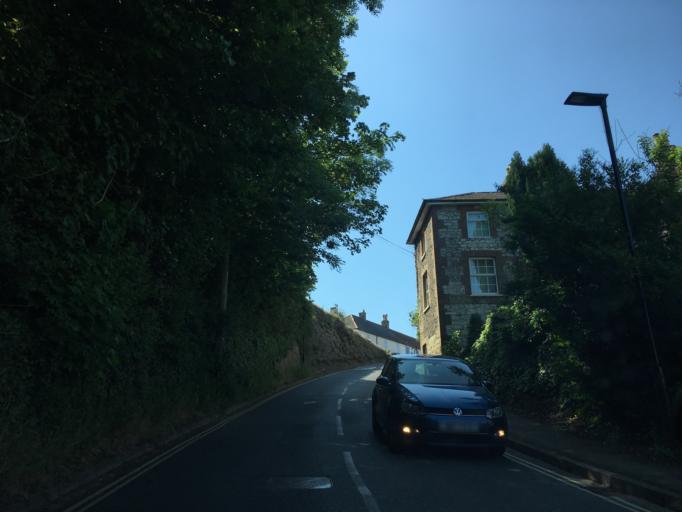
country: GB
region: England
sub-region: Isle of Wight
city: Newchurch
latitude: 50.6673
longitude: -1.2069
